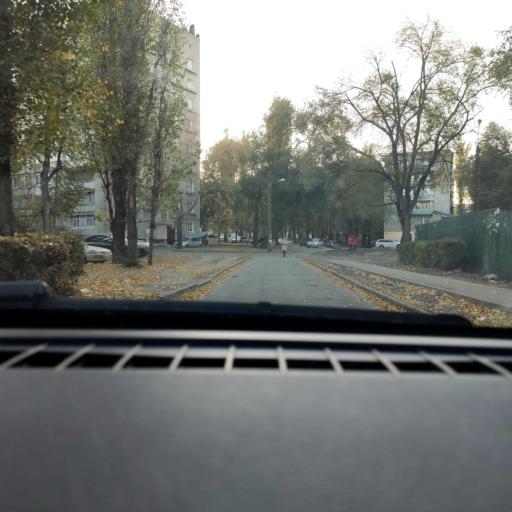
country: RU
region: Voronezj
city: Maslovka
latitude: 51.6130
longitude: 39.2500
